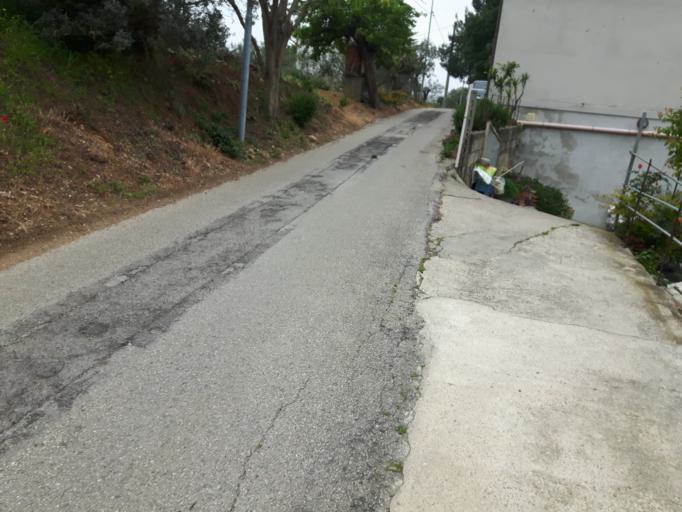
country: IT
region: Abruzzo
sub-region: Provincia di Chieti
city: Vasto
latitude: 42.1413
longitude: 14.6942
